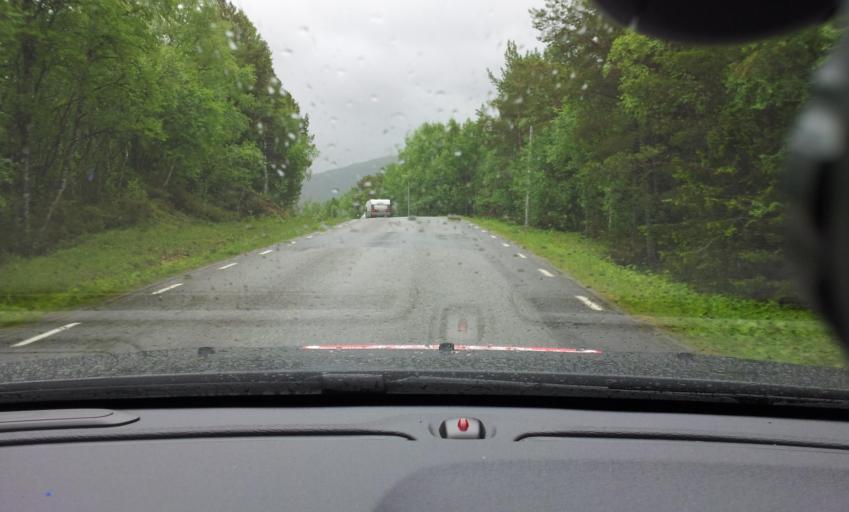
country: SE
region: Jaemtland
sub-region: Are Kommun
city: Are
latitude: 63.1469
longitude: 12.9746
